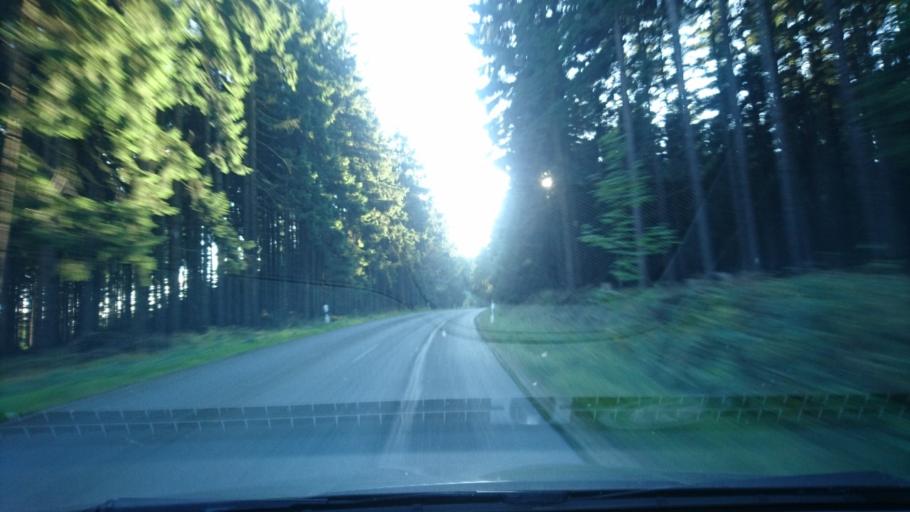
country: DE
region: Bavaria
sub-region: Upper Franconia
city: Issigau
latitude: 50.3591
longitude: 11.7487
